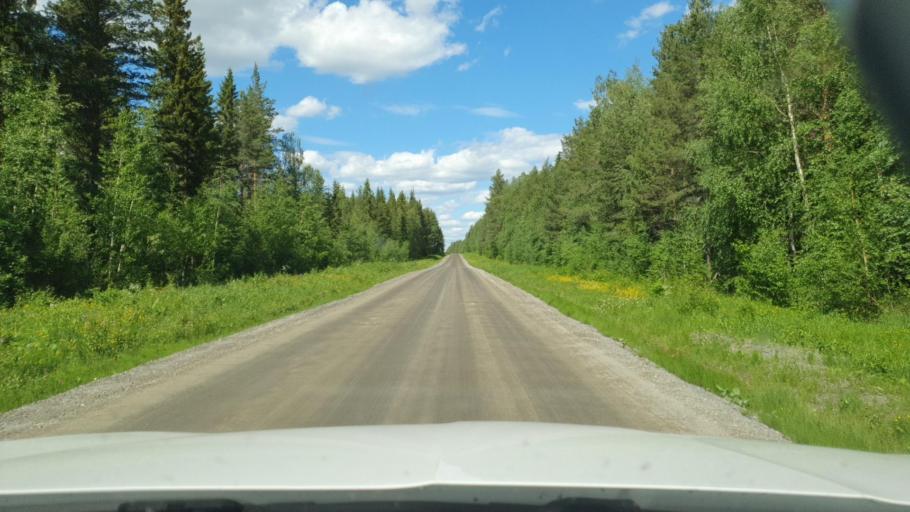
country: SE
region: Vaesterbotten
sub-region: Skelleftea Kommun
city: Forsbacka
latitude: 64.7701
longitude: 20.5174
